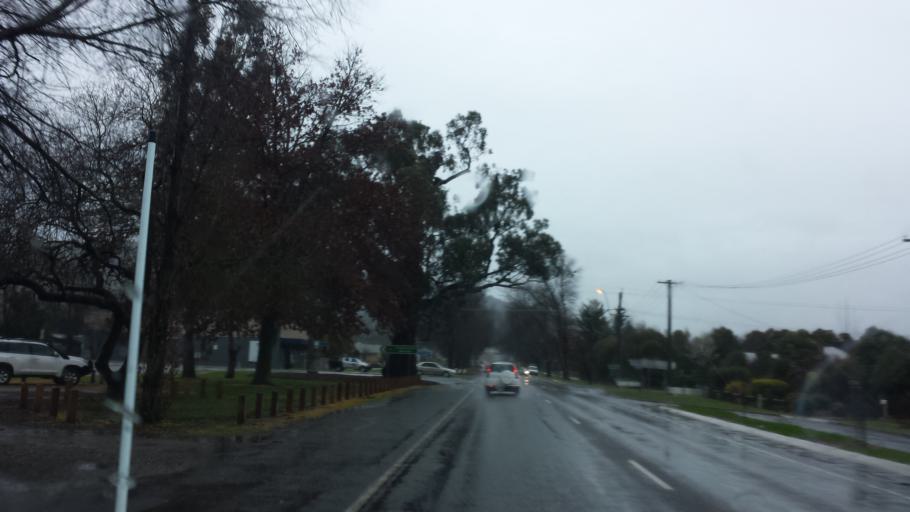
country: AU
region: Victoria
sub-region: Wangaratta
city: Wangaratta
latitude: -36.5579
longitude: 146.7190
